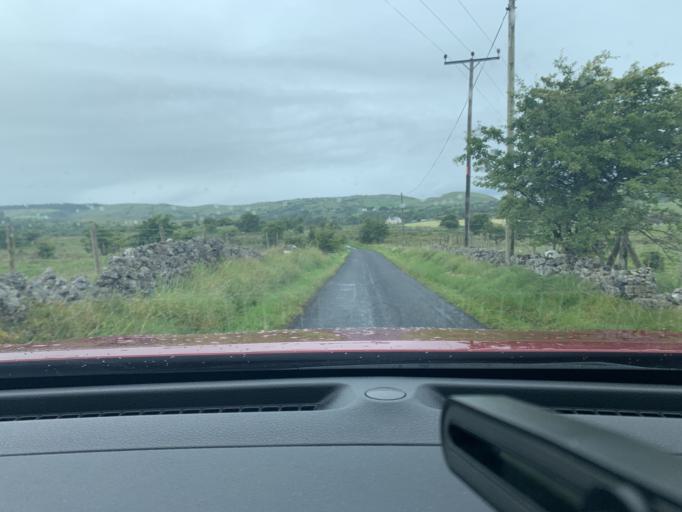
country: GB
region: Northern Ireland
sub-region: Fermanagh District
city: Enniskillen
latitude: 54.2562
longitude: -7.8408
